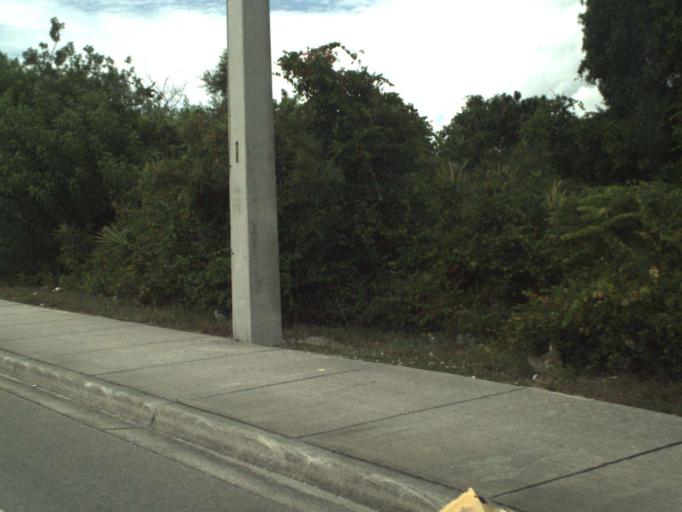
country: US
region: Florida
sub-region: Saint Lucie County
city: Fort Pierce North
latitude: 27.4743
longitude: -80.3498
